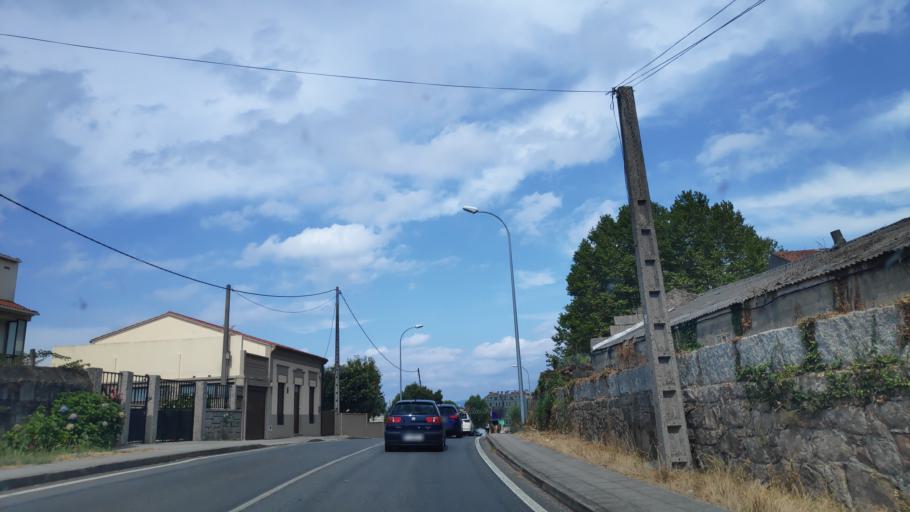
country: ES
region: Galicia
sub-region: Provincia de Pontevedra
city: Vilagarcia de Arousa
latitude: 42.5931
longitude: -8.7481
